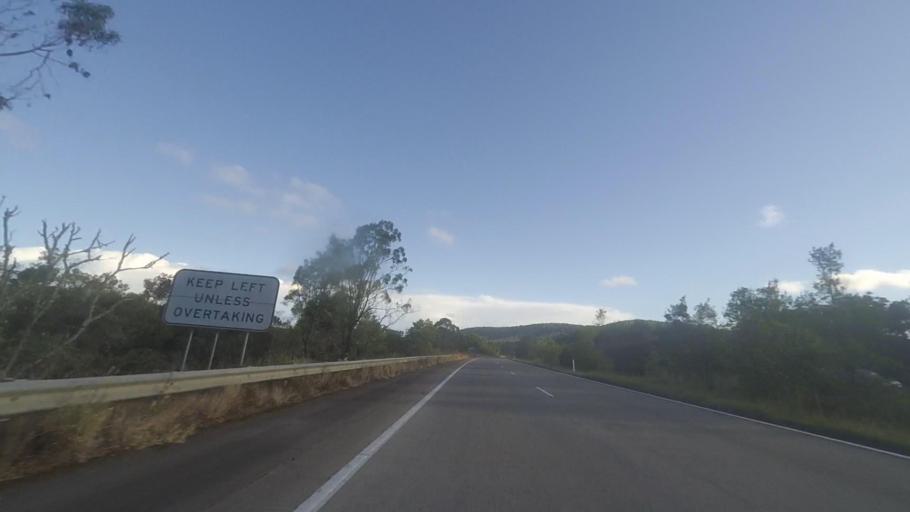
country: AU
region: New South Wales
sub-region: Great Lakes
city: Nabiac
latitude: -32.2627
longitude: 152.3276
